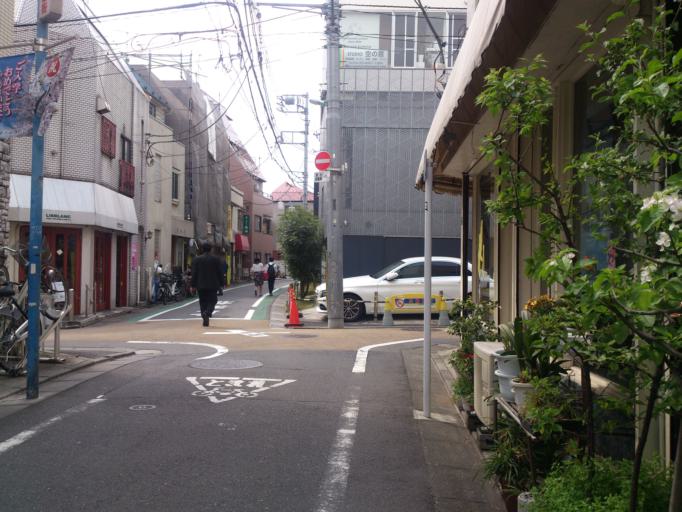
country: JP
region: Tokyo
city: Tokyo
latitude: 35.6578
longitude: 139.6864
